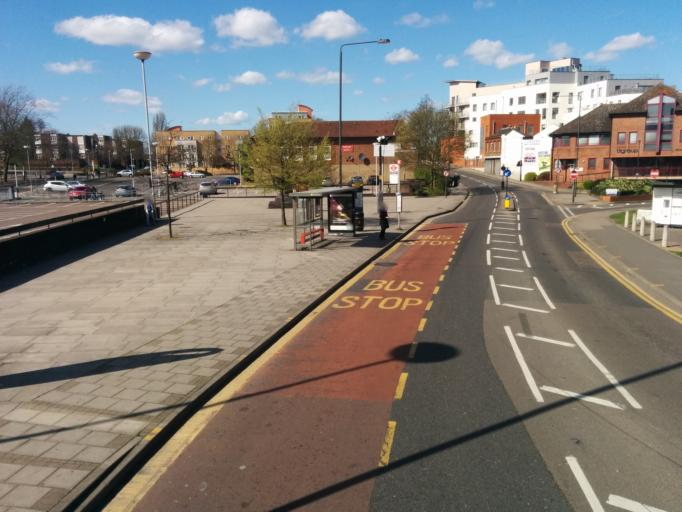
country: GB
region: England
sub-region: Greater London
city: Greenhill
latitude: 51.5892
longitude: -0.3328
